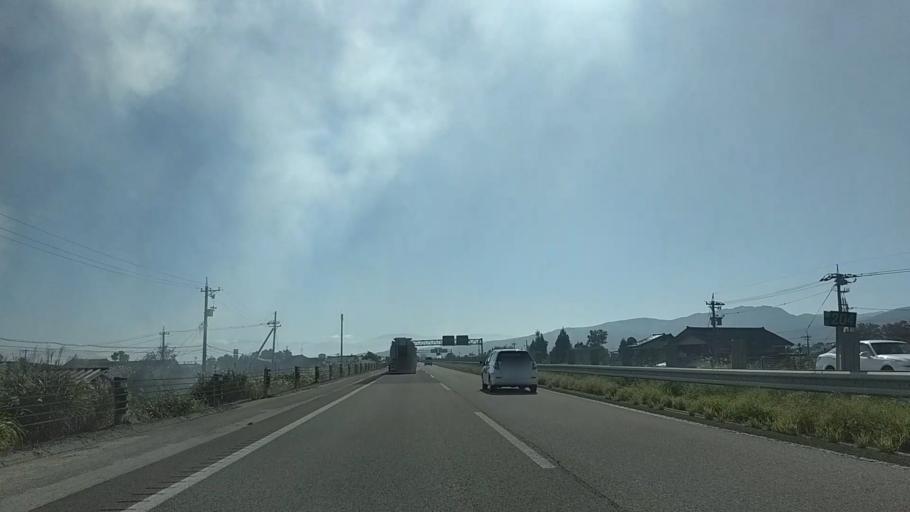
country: JP
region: Toyama
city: Nanto-shi
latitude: 36.6285
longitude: 136.9174
